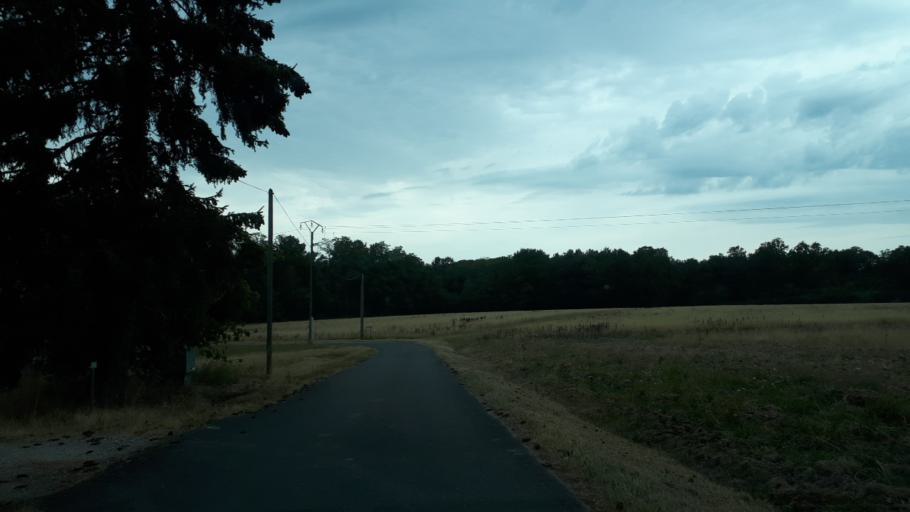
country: FR
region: Centre
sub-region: Departement du Loir-et-Cher
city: Saint-Romain-sur-Cher
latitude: 47.3559
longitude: 1.3985
